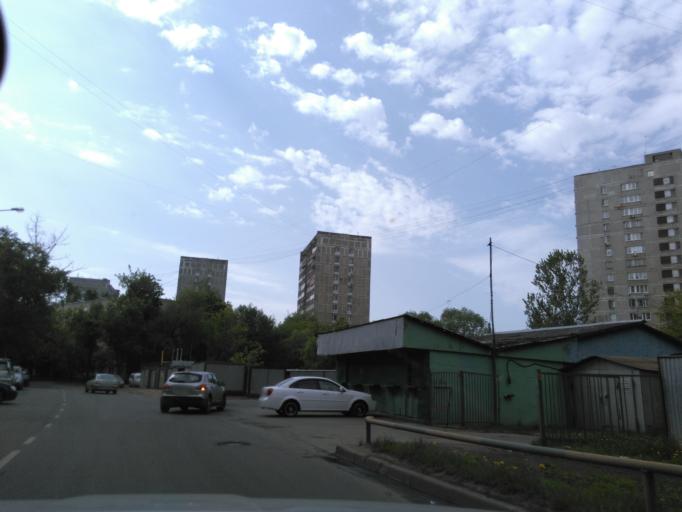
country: RU
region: Moscow
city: Novokhovrino
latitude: 55.8594
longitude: 37.5131
